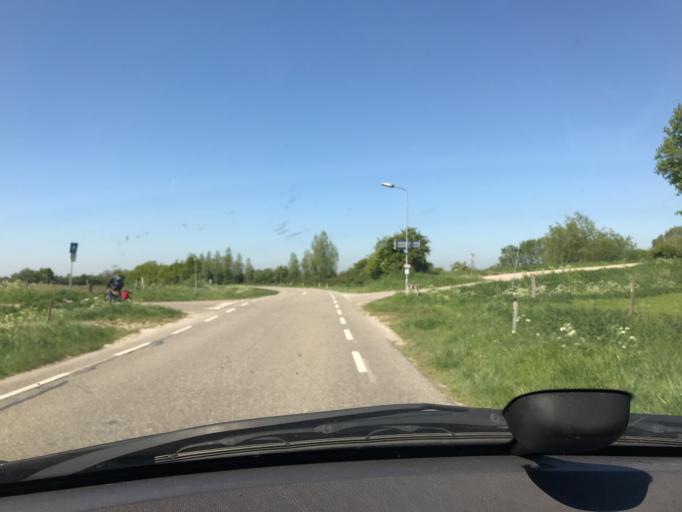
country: NL
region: Zeeland
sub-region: Gemeente Veere
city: Veere
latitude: 51.5136
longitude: 3.6875
